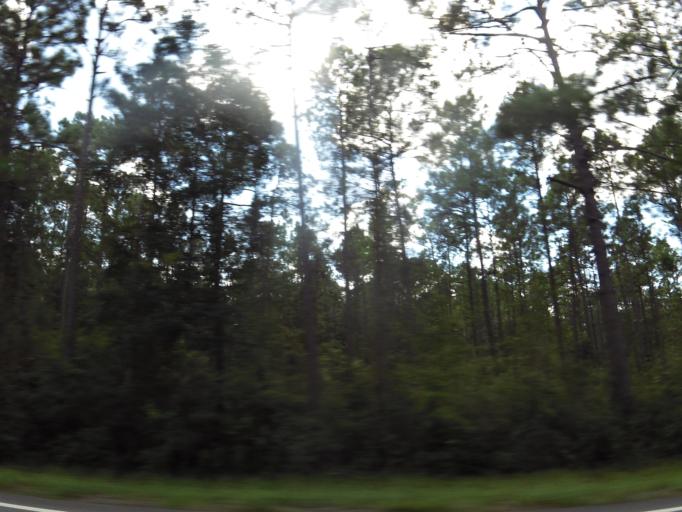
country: US
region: Georgia
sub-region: Echols County
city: Statenville
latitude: 30.7246
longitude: -83.0769
